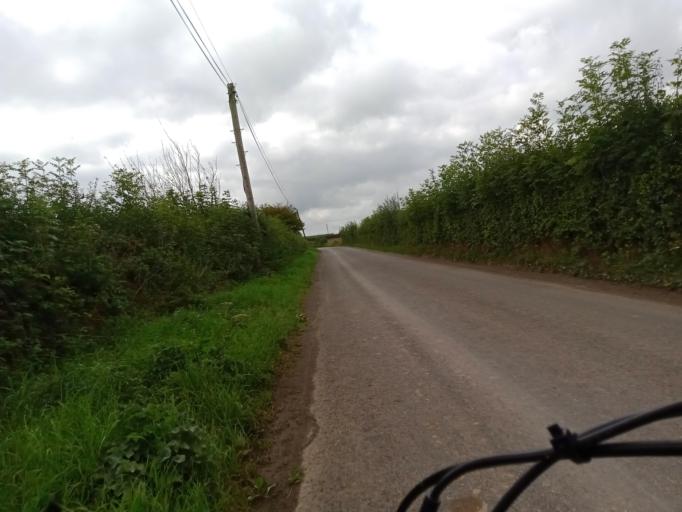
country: IE
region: Leinster
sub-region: Kilkenny
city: Callan
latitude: 52.5351
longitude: -7.2796
